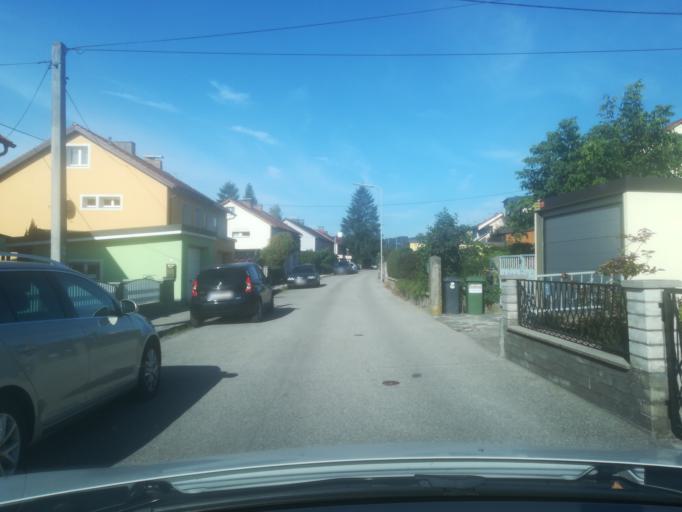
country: AT
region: Upper Austria
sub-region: Politischer Bezirk Linz-Land
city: Leonding
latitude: 48.2800
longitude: 14.2581
